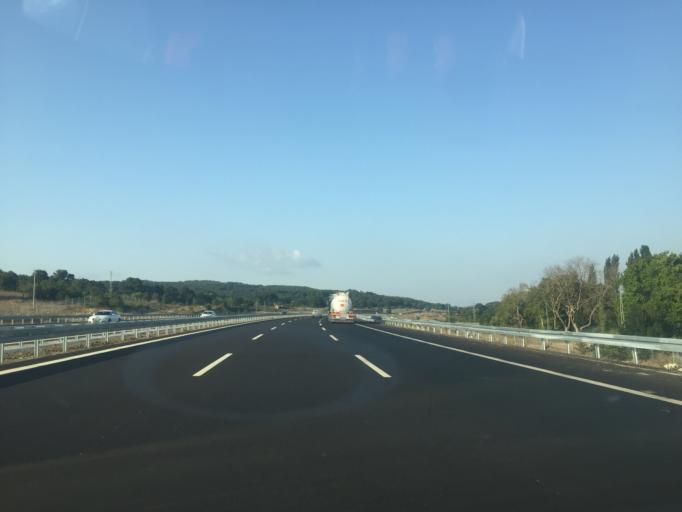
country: TR
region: Balikesir
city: Savastepe
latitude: 39.4821
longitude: 27.6515
